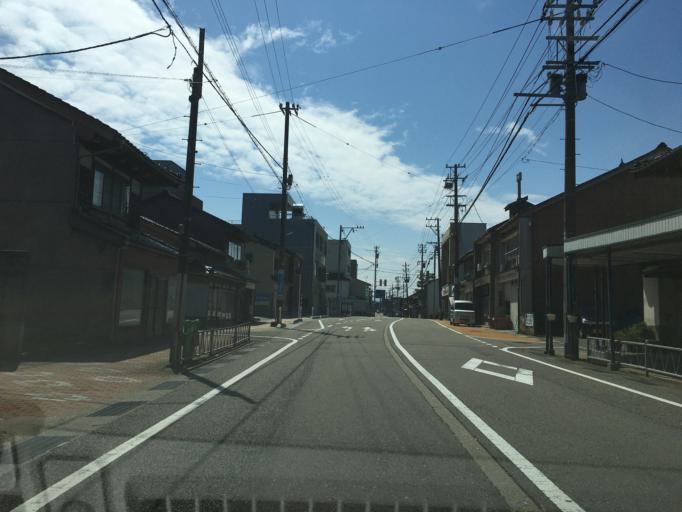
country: JP
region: Toyama
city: Himi
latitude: 36.8508
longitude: 136.9878
